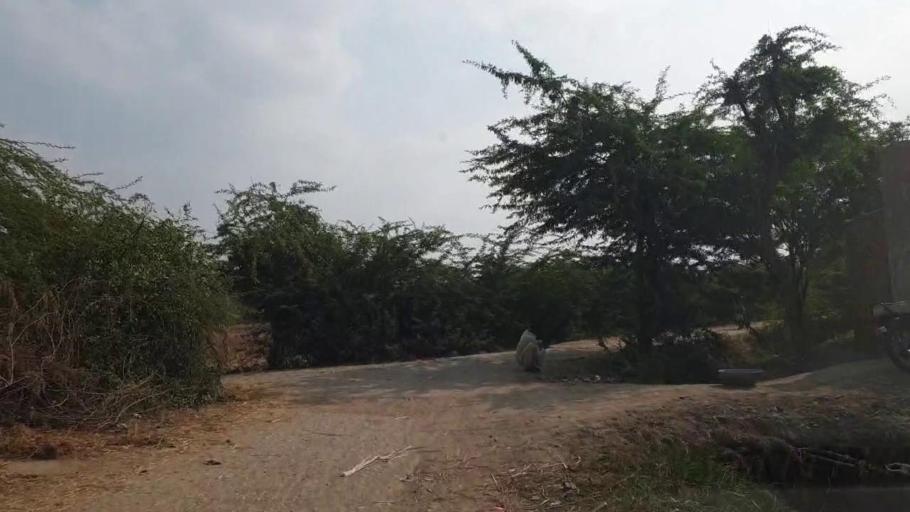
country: PK
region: Sindh
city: Rajo Khanani
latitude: 25.0428
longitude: 68.8028
